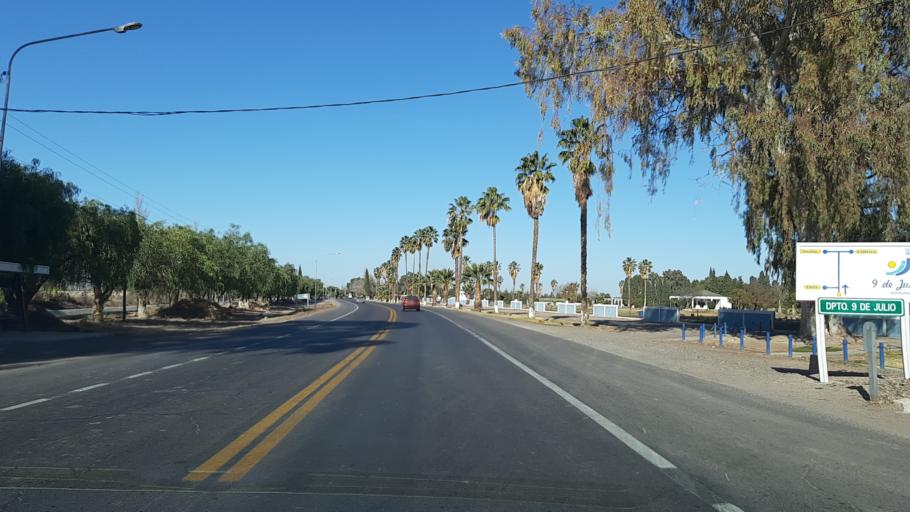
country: AR
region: San Juan
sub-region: Departamento de Santa Lucia
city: Santa Lucia
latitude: -31.5701
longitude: -68.4423
